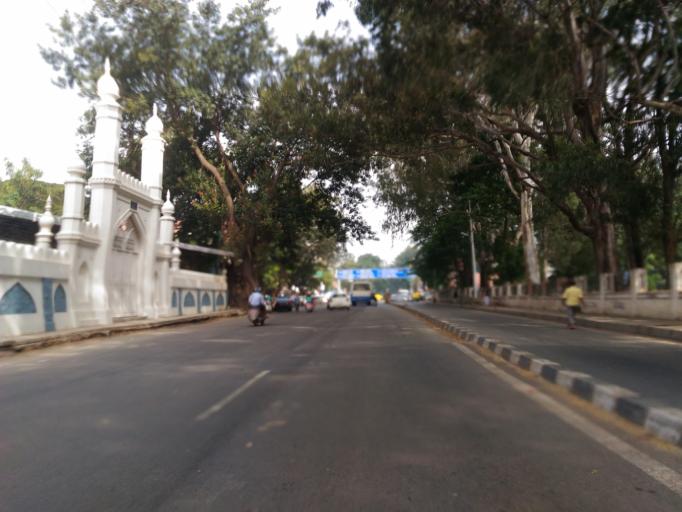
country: IN
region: Karnataka
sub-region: Bangalore Urban
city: Bangalore
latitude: 12.9634
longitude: 77.6068
